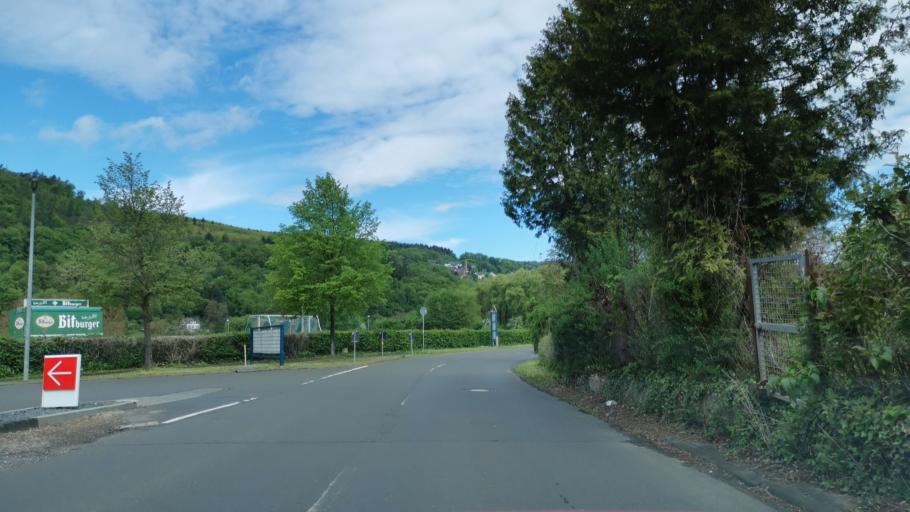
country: DE
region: Rheinland-Pfalz
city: Traben-Trarbach
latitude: 49.9572
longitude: 7.1053
